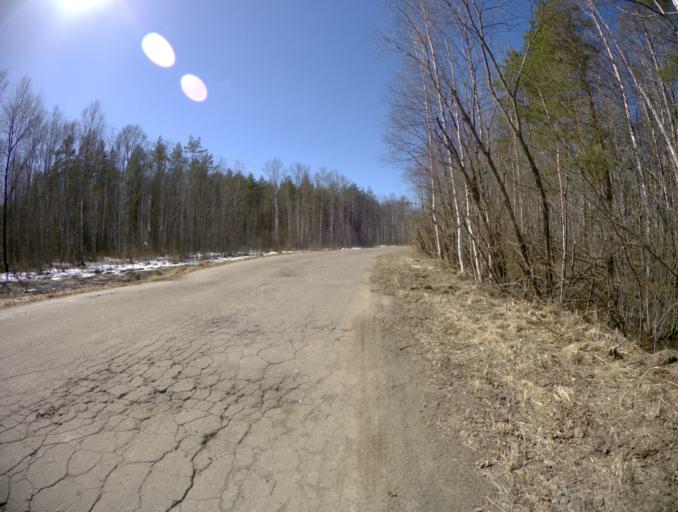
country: RU
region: Vladimir
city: Orgtrud
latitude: 56.2833
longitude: 40.7588
